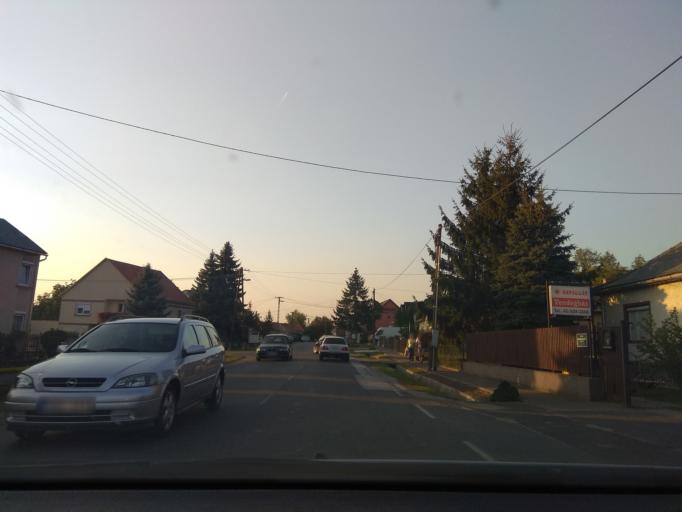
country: HU
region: Heves
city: Egerszalok
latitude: 47.8662
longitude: 20.3267
